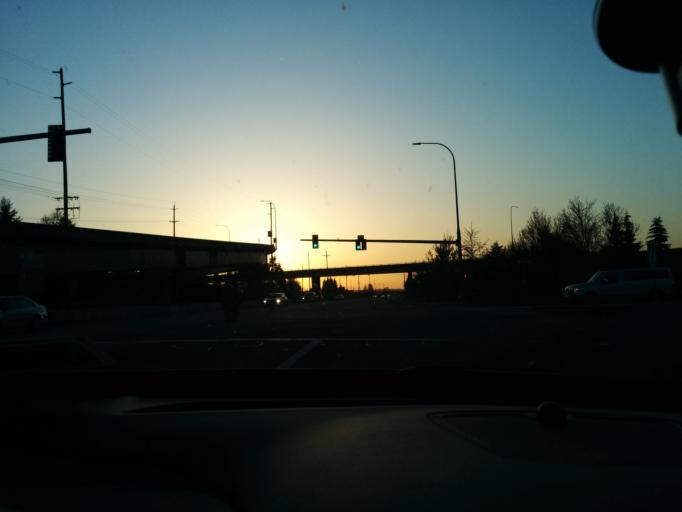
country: US
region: Washington
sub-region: Snohomish County
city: Monroe
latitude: 47.8621
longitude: -121.9811
